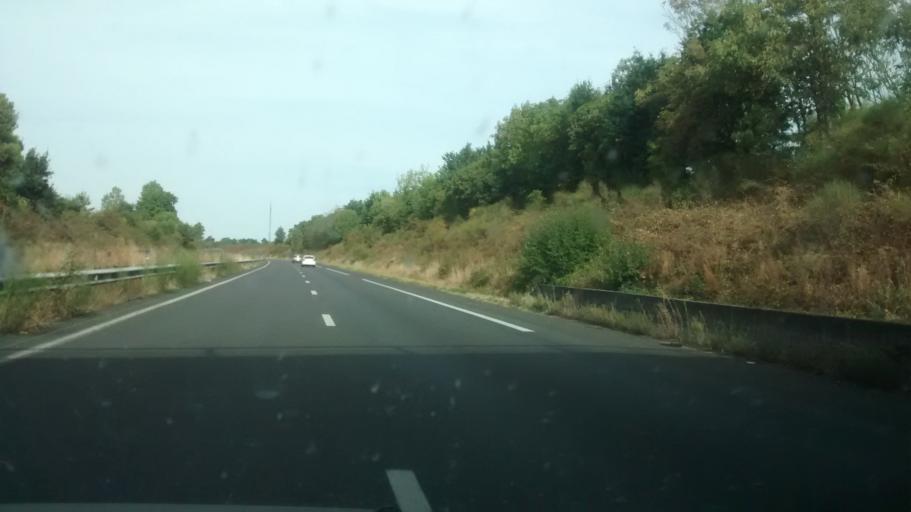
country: FR
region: Aquitaine
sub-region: Departement du Lot-et-Garonne
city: Meilhan-sur-Garonne
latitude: 44.4888
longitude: 0.0041
